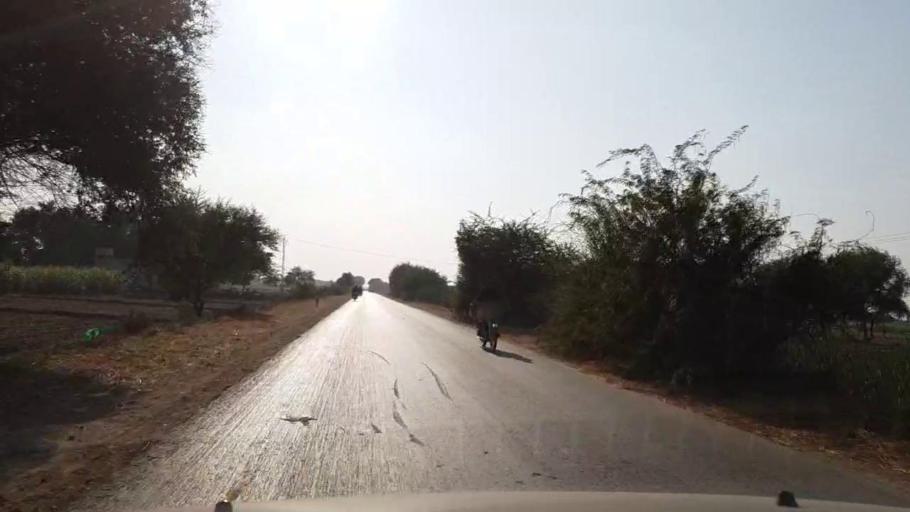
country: PK
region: Sindh
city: Tando Muhammad Khan
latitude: 25.0344
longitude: 68.4299
